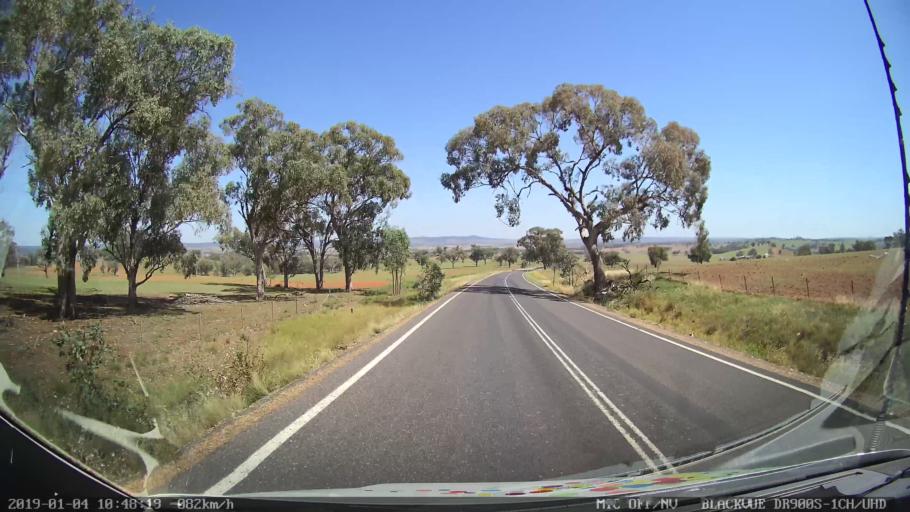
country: AU
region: New South Wales
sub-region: Cabonne
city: Molong
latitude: -33.2614
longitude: 148.7137
